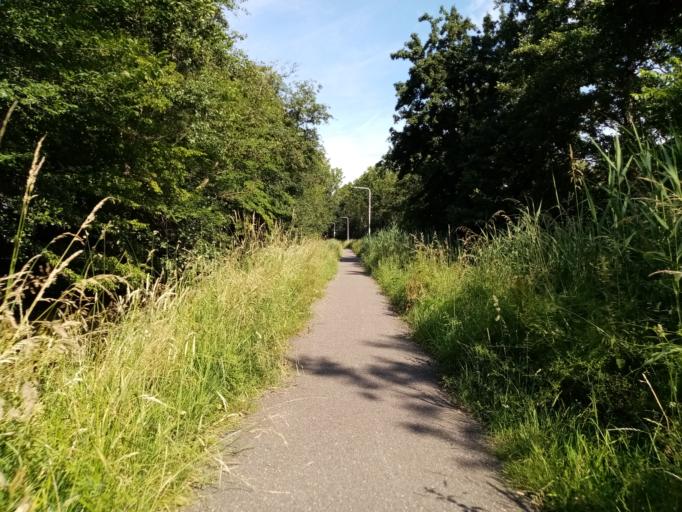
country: NL
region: South Holland
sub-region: Gemeente Oegstgeest
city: Oegstgeest
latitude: 52.1739
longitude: 4.4855
